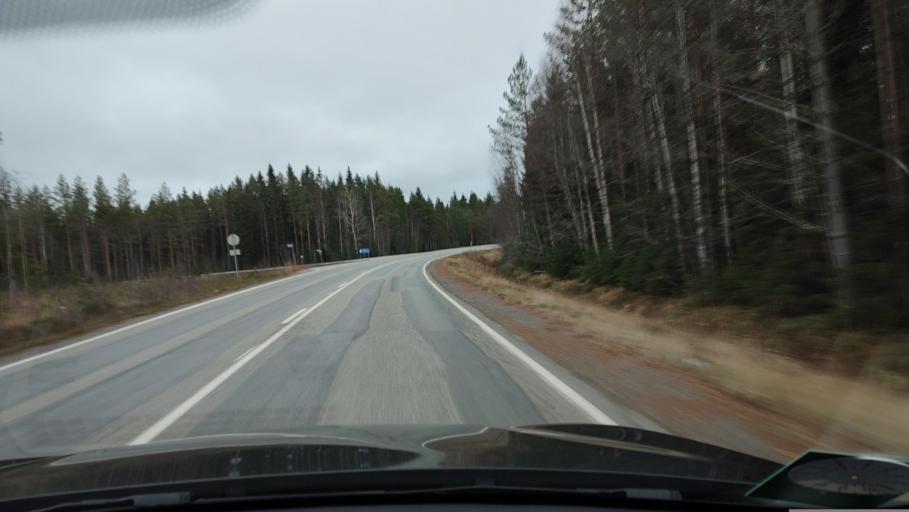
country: FI
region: Southern Ostrobothnia
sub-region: Suupohja
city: Karijoki
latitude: 62.2309
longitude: 21.7320
